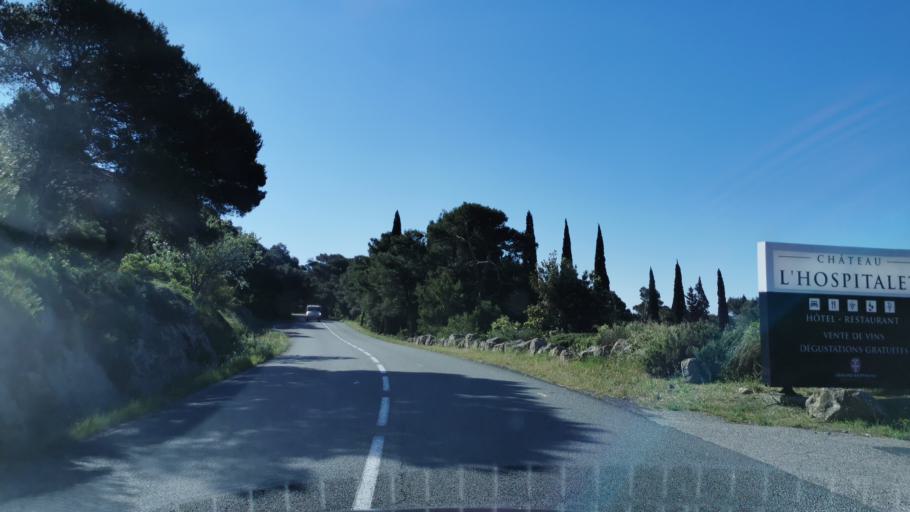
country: FR
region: Languedoc-Roussillon
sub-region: Departement de l'Aude
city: Armissan
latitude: 43.1698
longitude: 3.1150
